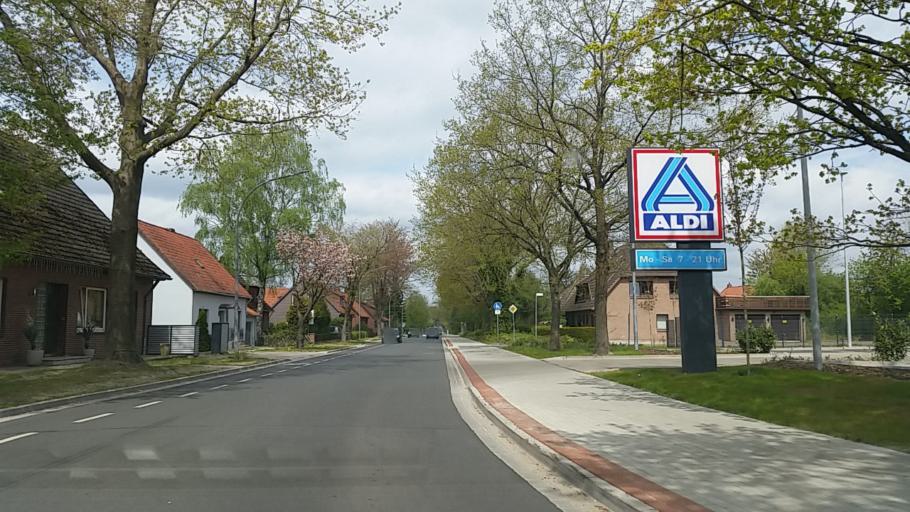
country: DE
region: Lower Saxony
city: Schneverdingen
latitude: 53.1203
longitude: 9.7816
